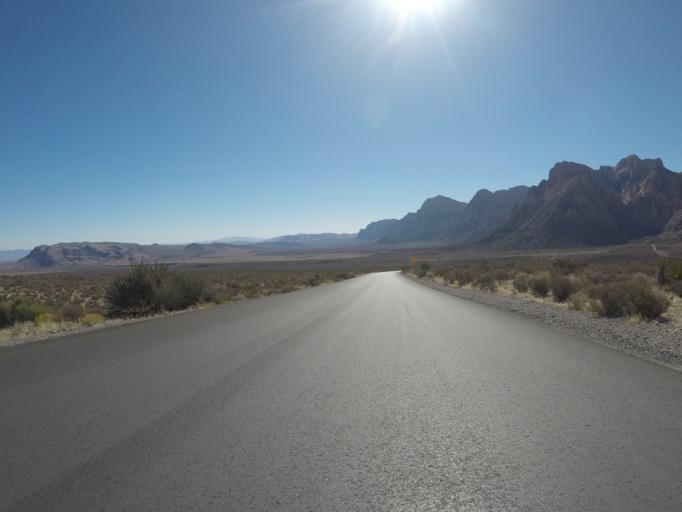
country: US
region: Nevada
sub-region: Clark County
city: Summerlin South
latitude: 36.1652
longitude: -115.4757
